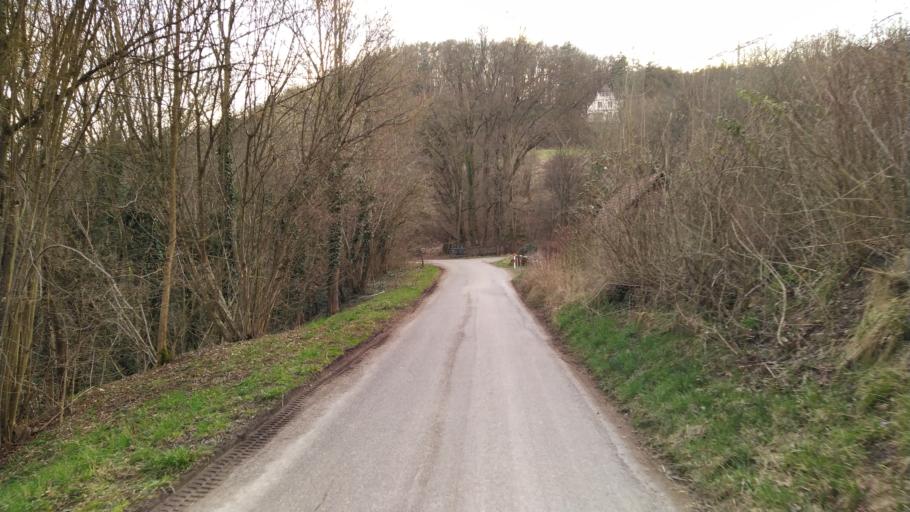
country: DE
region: Baden-Wuerttemberg
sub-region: Tuebingen Region
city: Tuebingen
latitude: 48.5076
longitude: 9.0304
